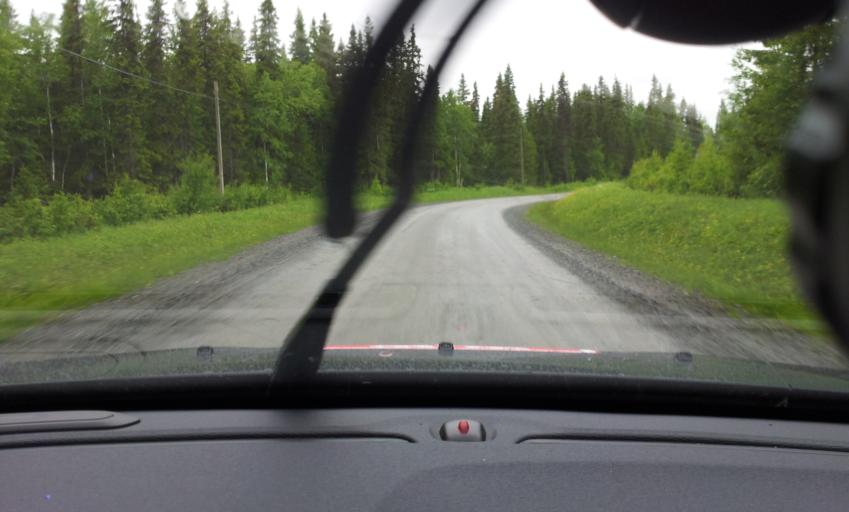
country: SE
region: Jaemtland
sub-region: Are Kommun
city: Are
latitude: 63.4453
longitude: 12.8050
